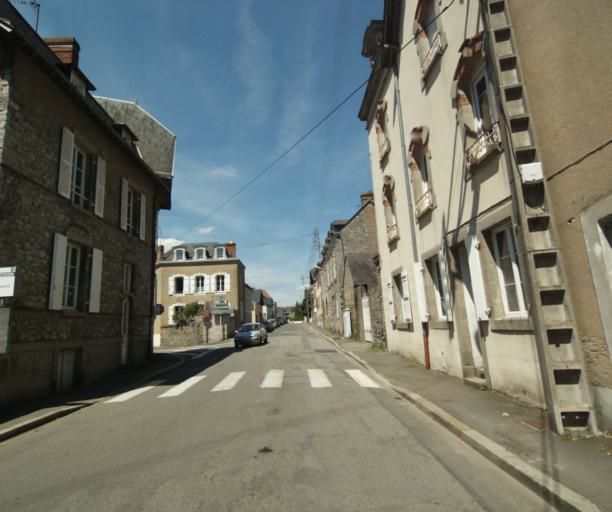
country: FR
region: Pays de la Loire
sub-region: Departement de la Mayenne
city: Laval
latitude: 48.0768
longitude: -0.7651
